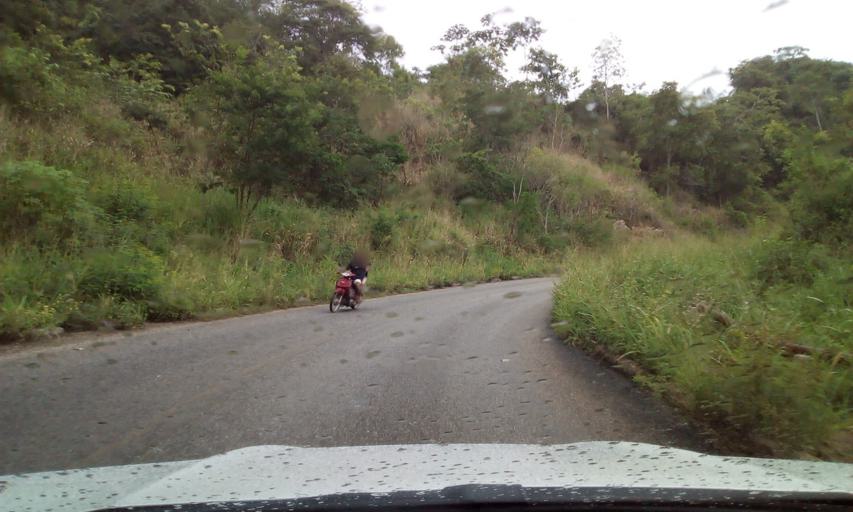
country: BR
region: Paraiba
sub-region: Areia
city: Areia
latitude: -6.8889
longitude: -35.6475
